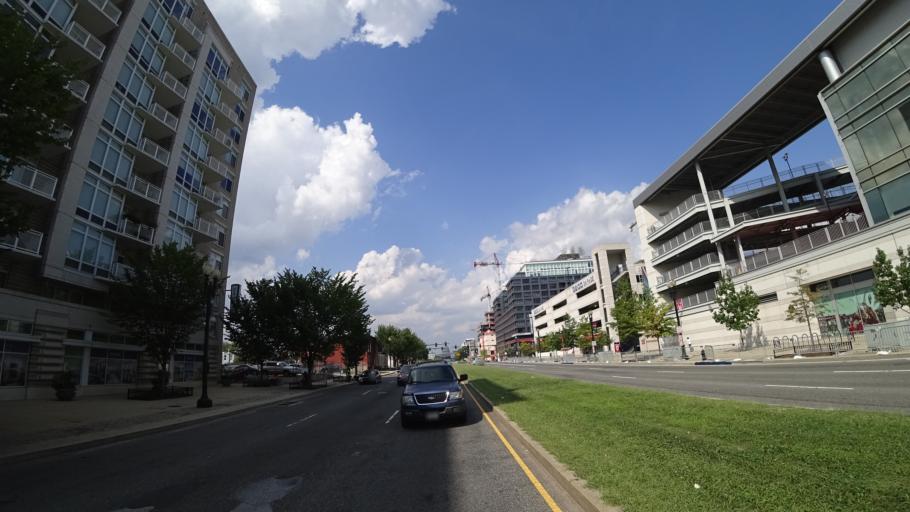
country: US
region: Washington, D.C.
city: Washington, D.C.
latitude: 38.8735
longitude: -77.0091
